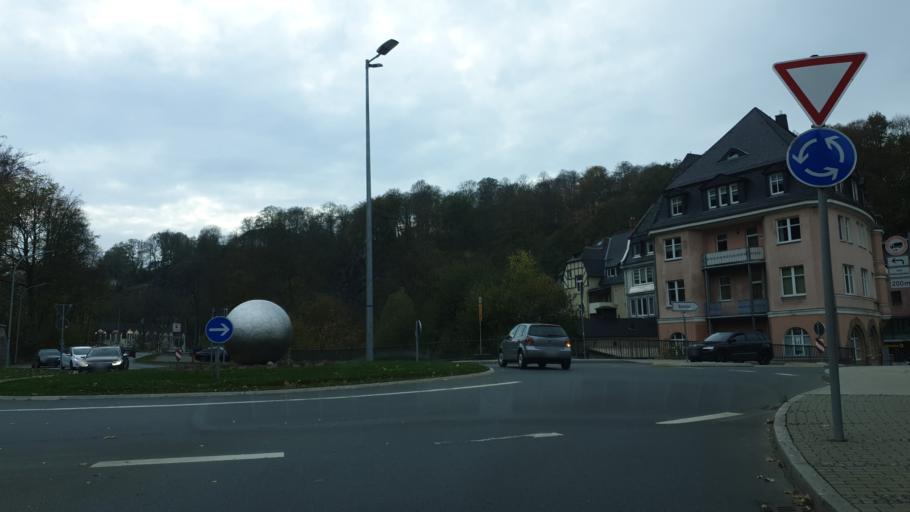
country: DE
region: Saxony
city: Schwarzenberg
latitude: 50.5419
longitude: 12.7886
